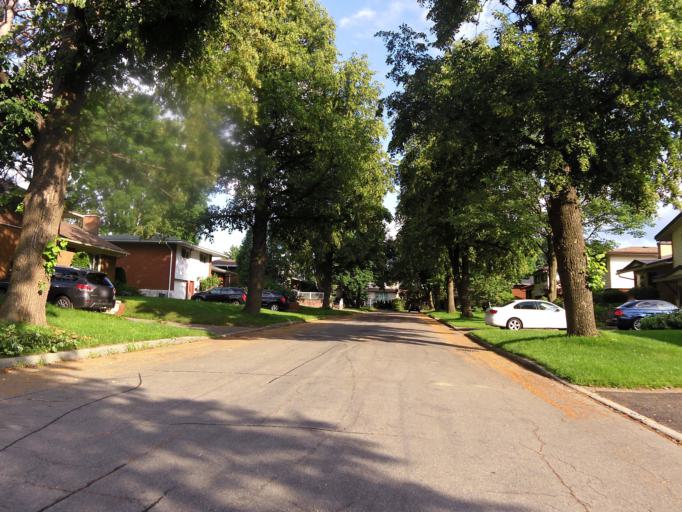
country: CA
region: Ontario
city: Bells Corners
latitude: 45.3482
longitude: -75.7831
